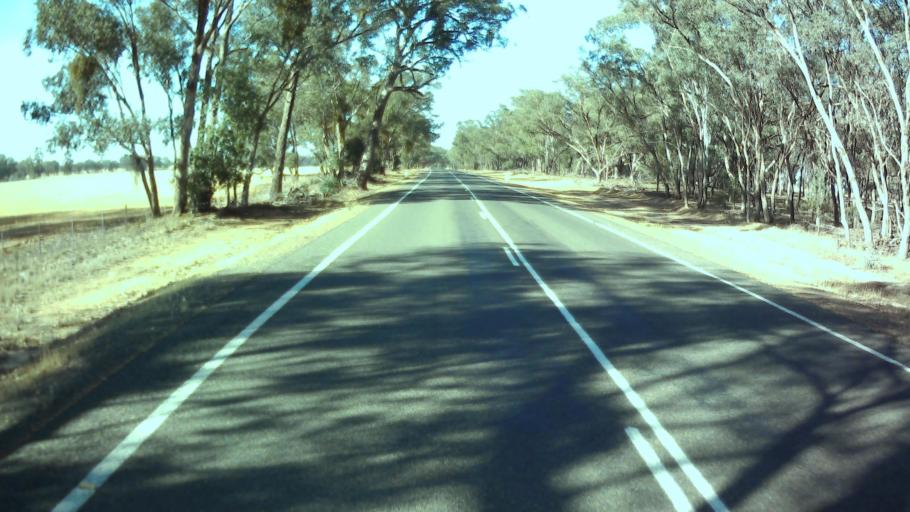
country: AU
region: New South Wales
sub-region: Weddin
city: Grenfell
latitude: -34.0041
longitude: 148.1250
